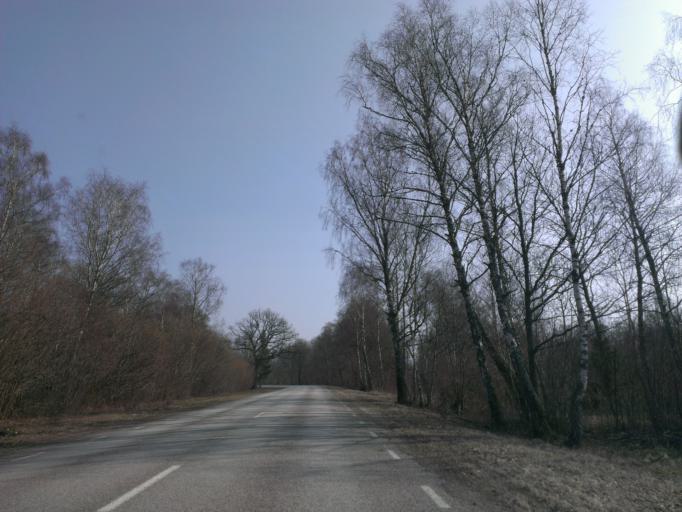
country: EE
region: Saare
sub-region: Kuressaare linn
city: Kuressaare
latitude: 58.2756
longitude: 22.6294
